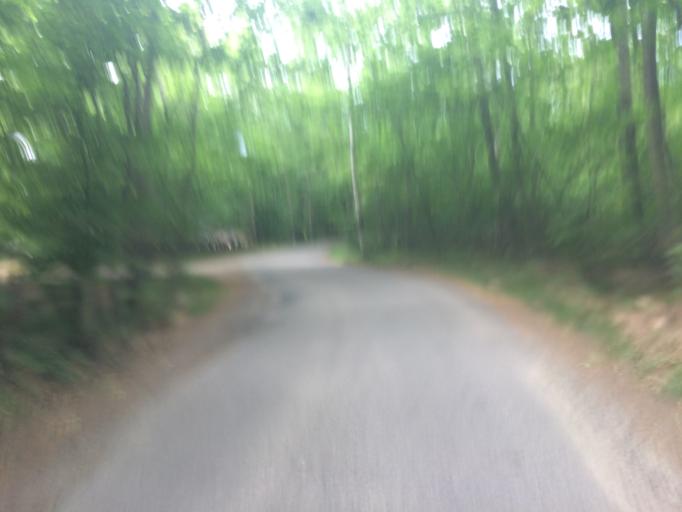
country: DK
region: Capital Region
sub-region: Bornholm Kommune
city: Ronne
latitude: 55.1689
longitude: 14.7160
